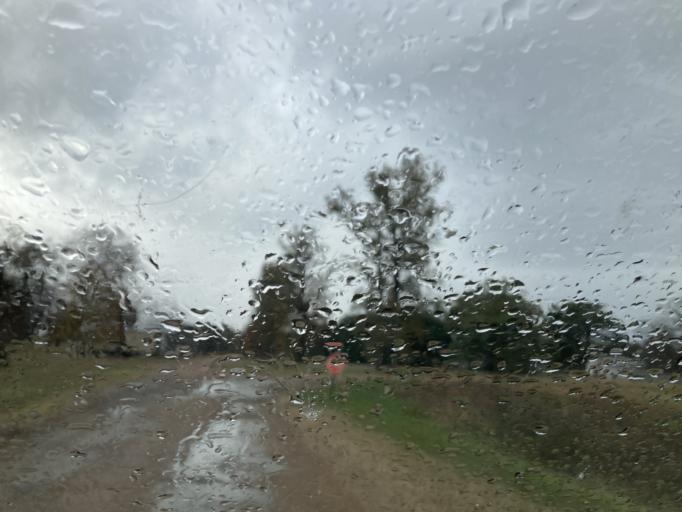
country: US
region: Mississippi
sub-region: Yazoo County
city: Yazoo City
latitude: 32.9879
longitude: -90.4478
